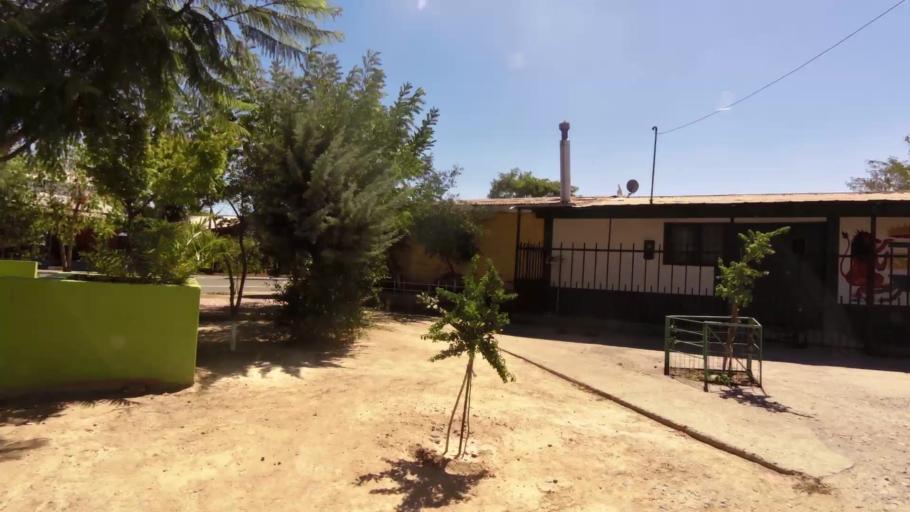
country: CL
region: O'Higgins
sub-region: Provincia de Colchagua
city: Chimbarongo
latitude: -34.5762
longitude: -70.9878
